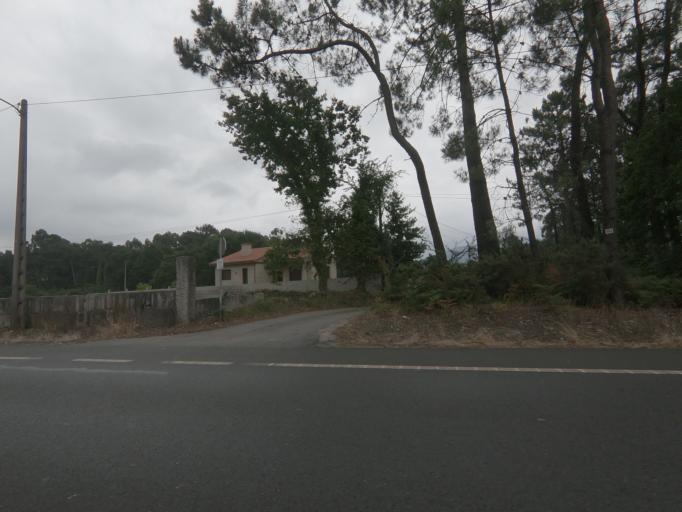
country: ES
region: Galicia
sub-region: Provincia de Pontevedra
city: Tomino
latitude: 41.9769
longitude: -8.7375
